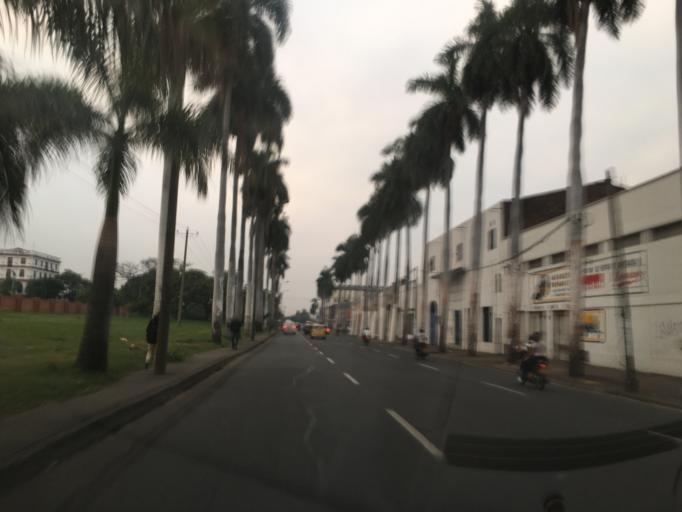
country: CO
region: Valle del Cauca
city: Cali
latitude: 3.4558
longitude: -76.5199
